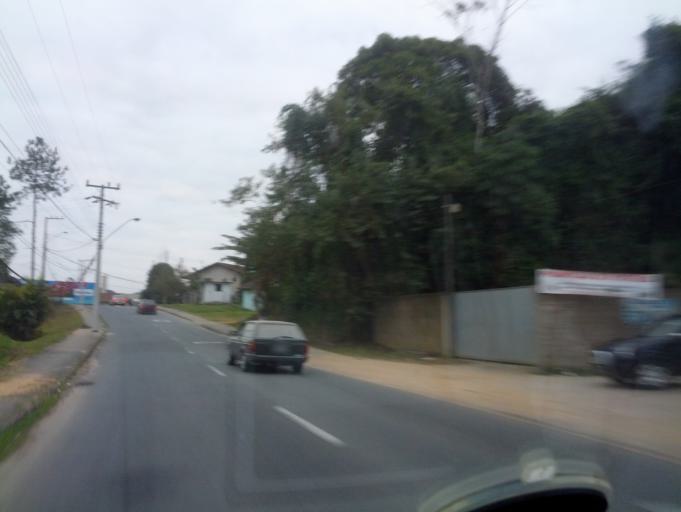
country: BR
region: Santa Catarina
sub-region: Blumenau
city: Blumenau
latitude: -26.8739
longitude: -49.0827
